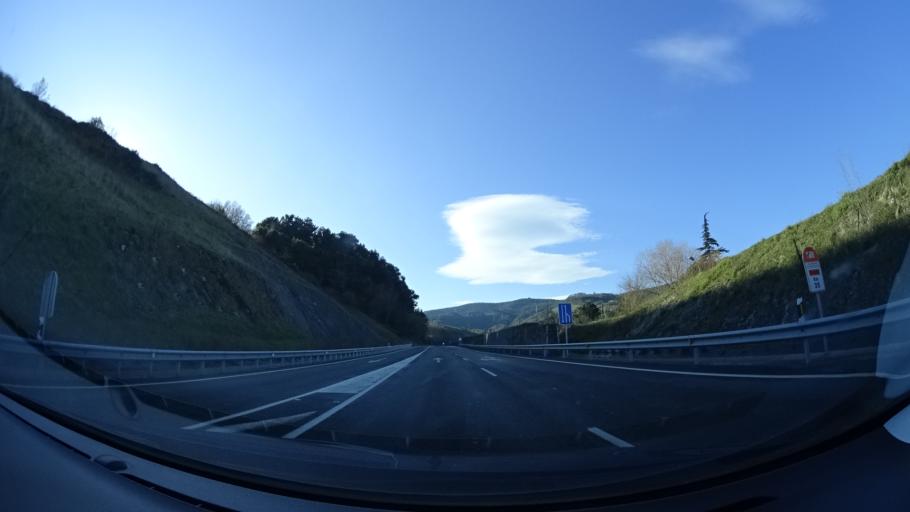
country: ES
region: Basque Country
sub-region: Bizkaia
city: Bermeo
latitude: 43.4192
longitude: -2.7374
